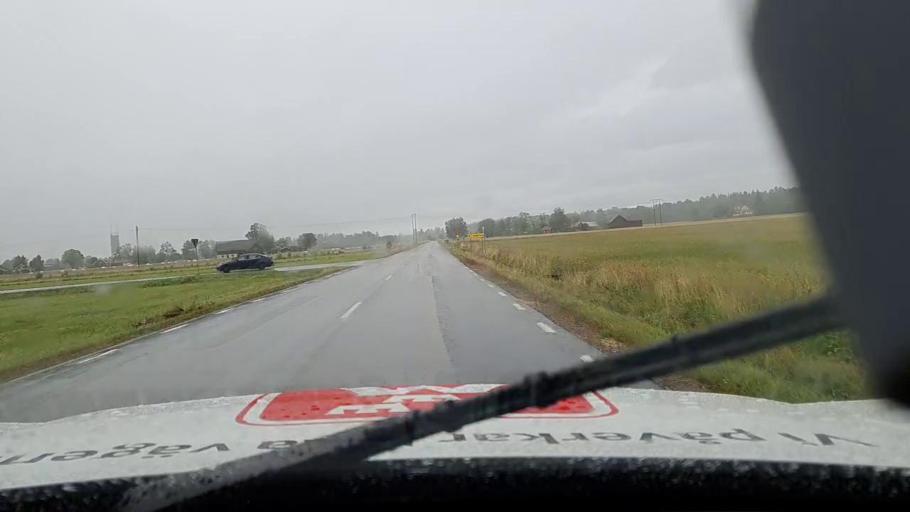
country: SE
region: Vaestra Goetaland
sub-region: Toreboda Kommun
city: Toereboda
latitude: 58.6915
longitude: 14.1286
